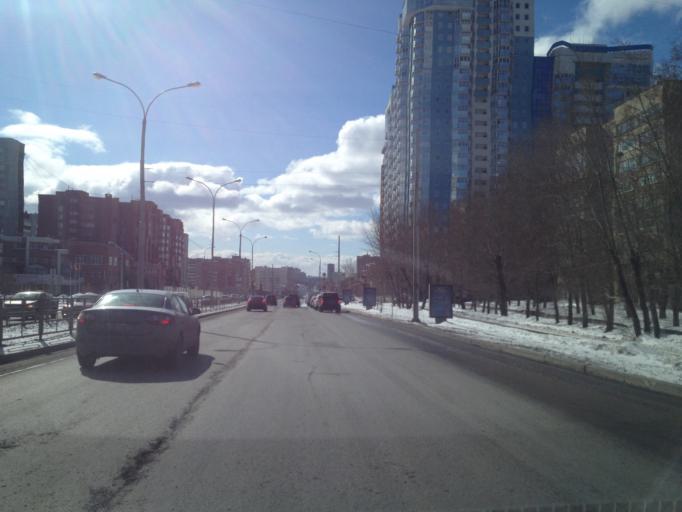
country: RU
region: Sverdlovsk
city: Yekaterinburg
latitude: 56.8242
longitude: 60.5861
